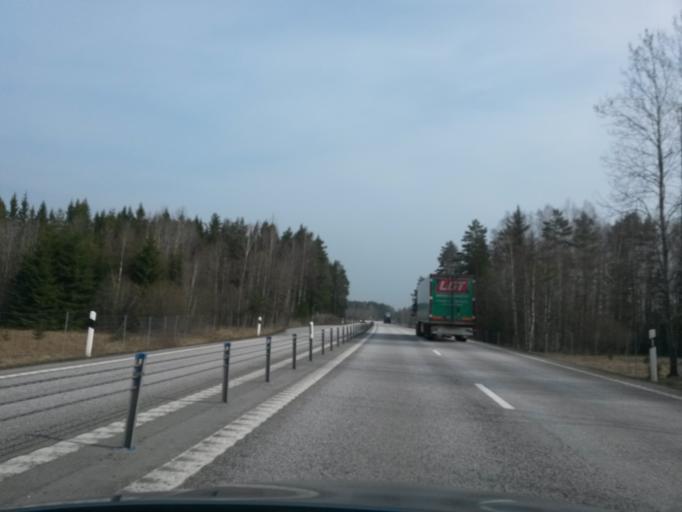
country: SE
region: Vaestra Goetaland
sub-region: Gullspangs Kommun
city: Hova
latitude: 58.8136
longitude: 14.1333
